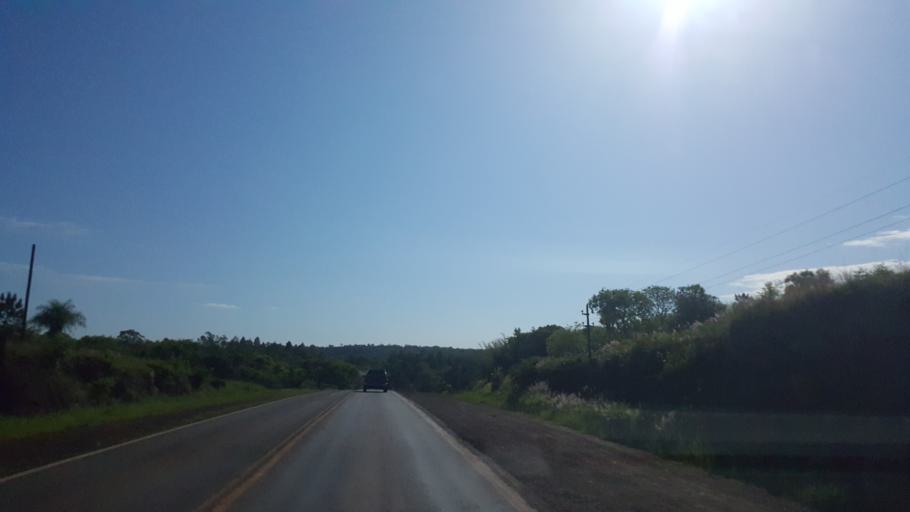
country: AR
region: Misiones
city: Santa Ana
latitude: -27.3707
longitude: -55.5656
